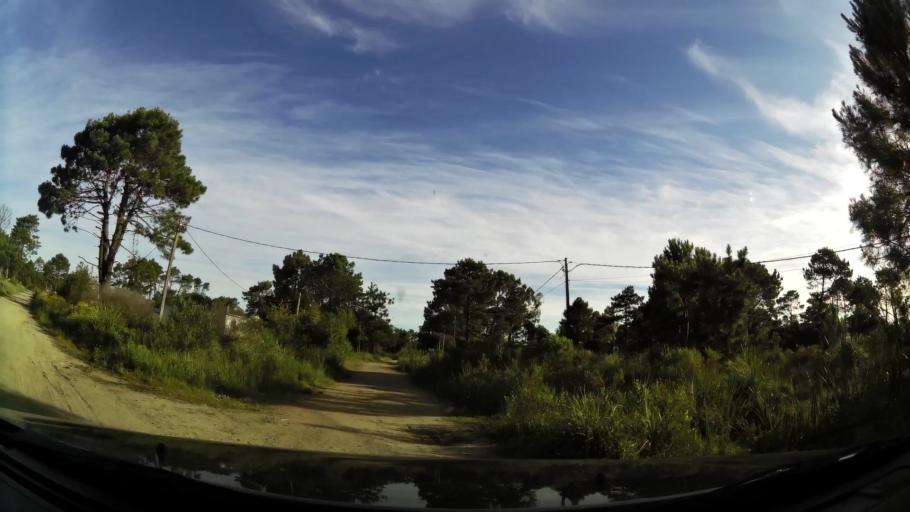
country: UY
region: Canelones
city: Empalme Olmos
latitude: -34.7669
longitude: -55.8633
